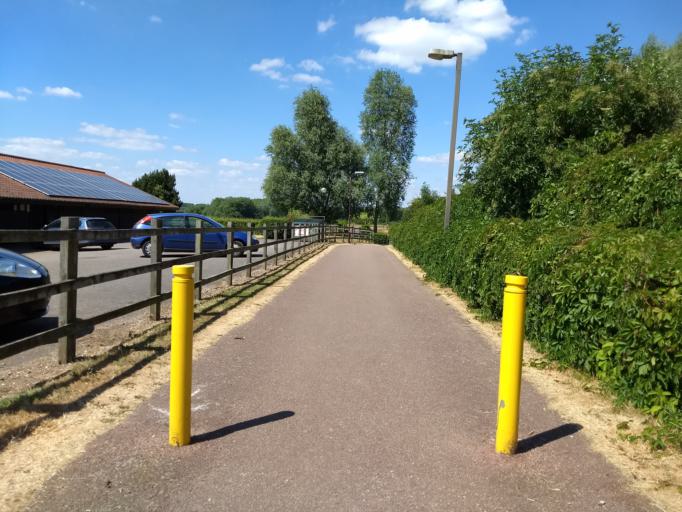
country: GB
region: England
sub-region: Milton Keynes
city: Simpson
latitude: 52.0057
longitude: -0.7026
